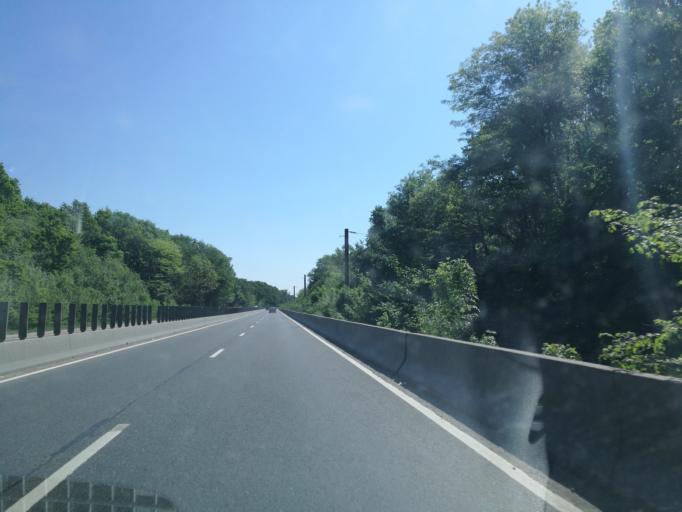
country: RO
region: Ilfov
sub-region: Comuna Tunari
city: Tunari
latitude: 44.5392
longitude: 26.1155
